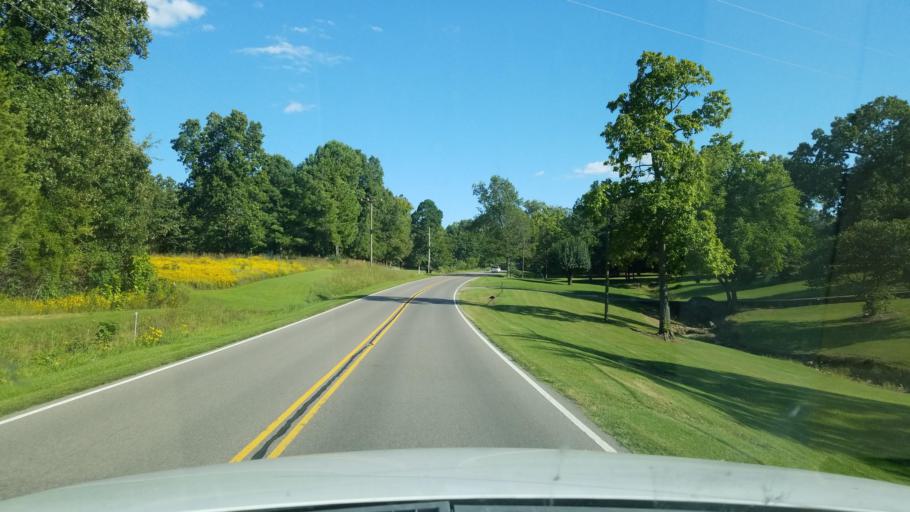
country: US
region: Illinois
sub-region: Saline County
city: Harrisburg
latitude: 37.6321
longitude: -88.4785
